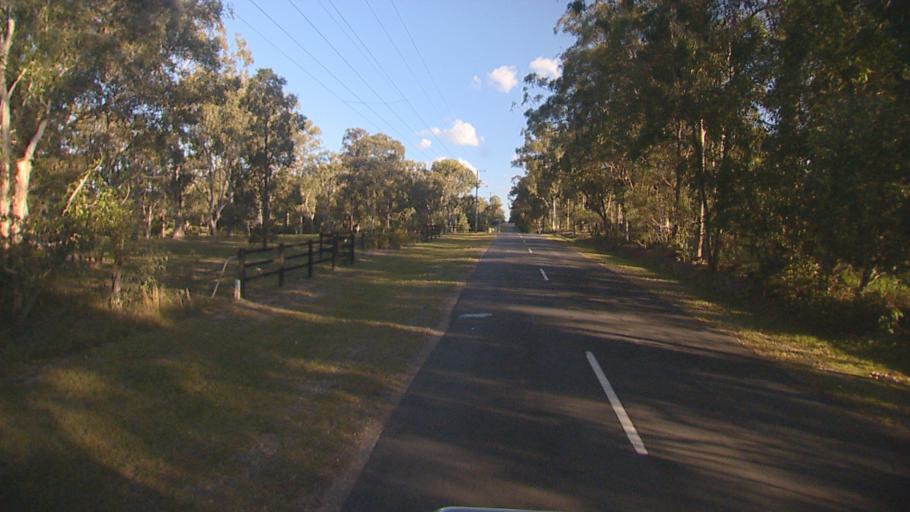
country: AU
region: Queensland
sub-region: Redland
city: Redland Bay
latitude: -27.6743
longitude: 153.2763
